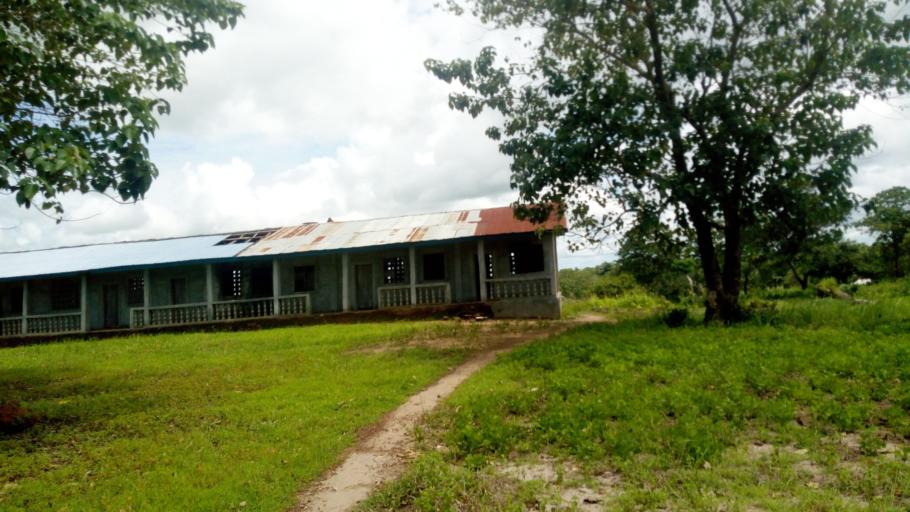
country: SL
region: Northern Province
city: Magburaka
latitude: 8.7127
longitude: -11.9547
